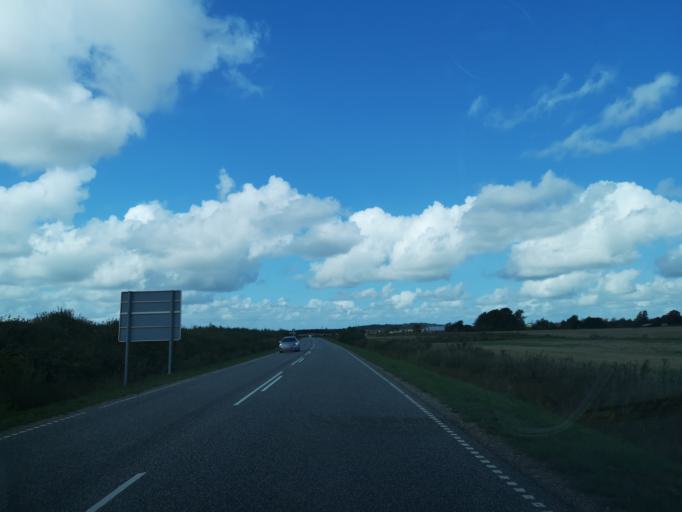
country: DK
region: Central Jutland
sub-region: Holstebro Kommune
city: Holstebro
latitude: 56.3898
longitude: 8.5958
